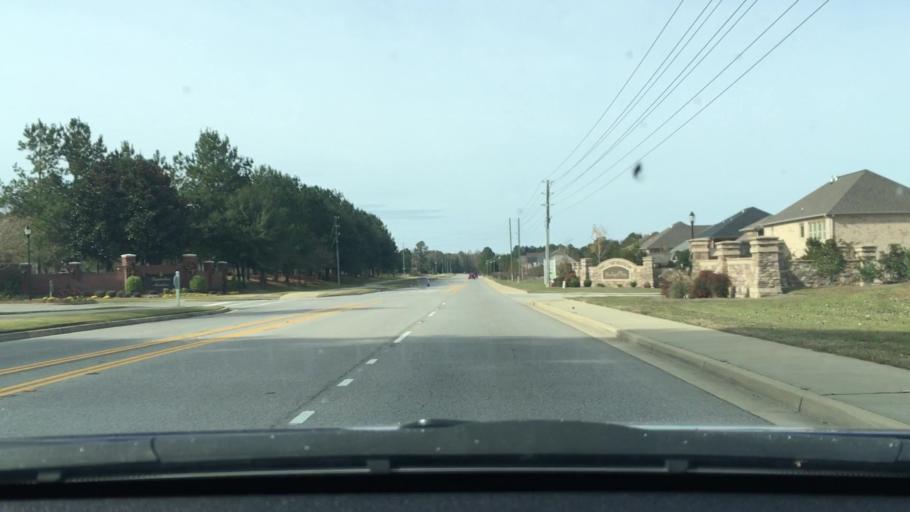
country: US
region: South Carolina
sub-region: Sumter County
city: Cane Savannah
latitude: 33.9300
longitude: -80.4118
